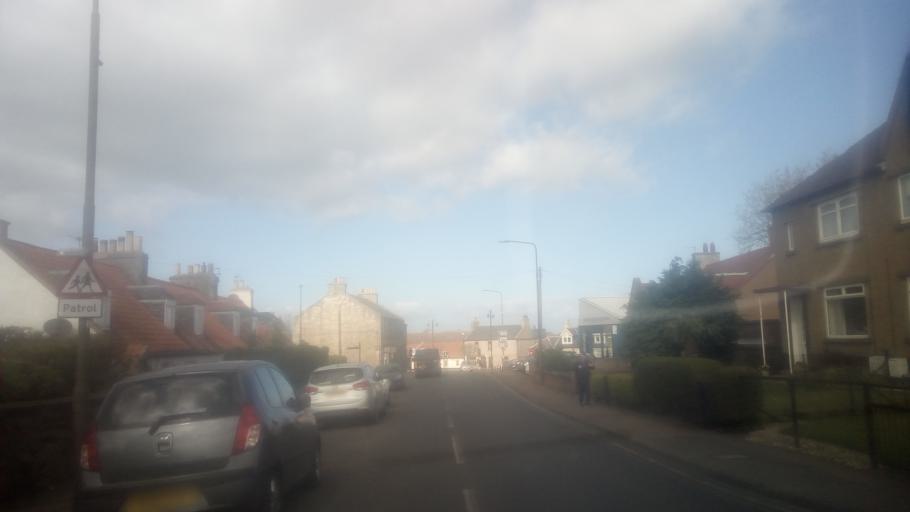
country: GB
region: Scotland
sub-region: East Lothian
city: Tranent
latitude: 55.9423
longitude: -2.9487
